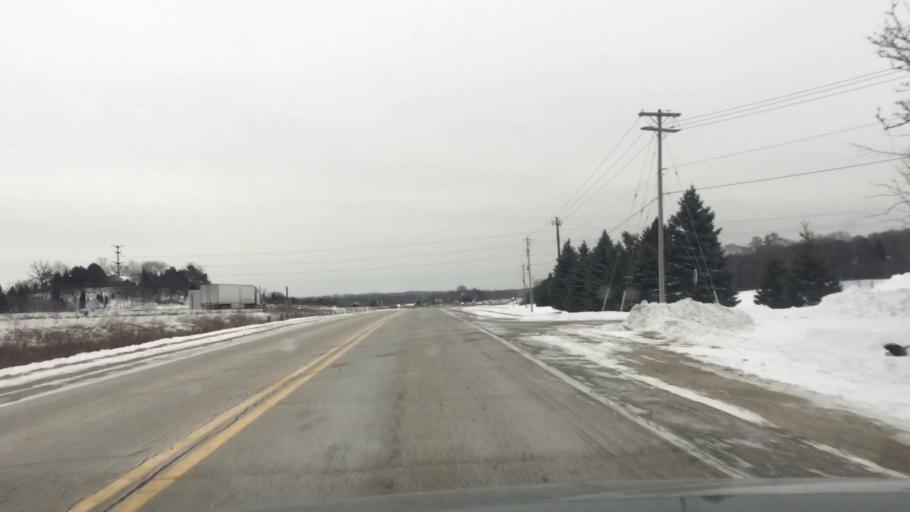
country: US
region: Wisconsin
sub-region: Waukesha County
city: Wales
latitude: 43.0485
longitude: -88.3487
